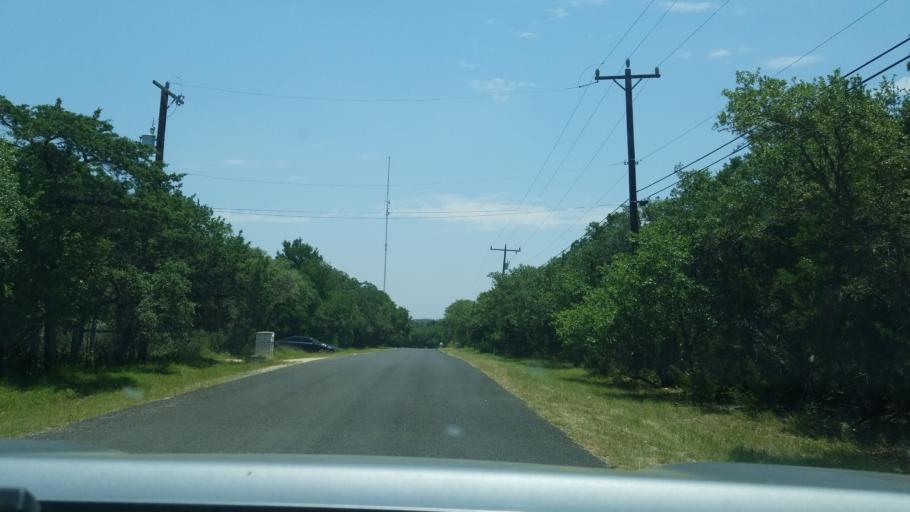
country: US
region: Texas
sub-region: Bexar County
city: Timberwood Park
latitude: 29.6973
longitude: -98.5200
